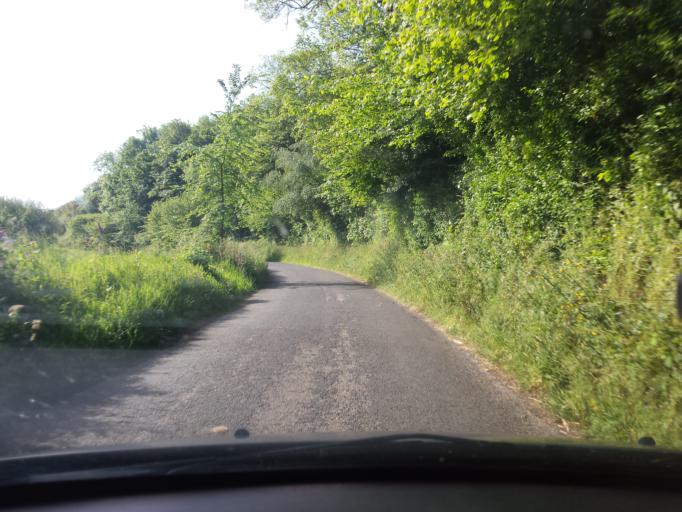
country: FR
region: Lower Normandy
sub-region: Departement de la Manche
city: Beaumont-Hague
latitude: 49.6833
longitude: -1.9227
